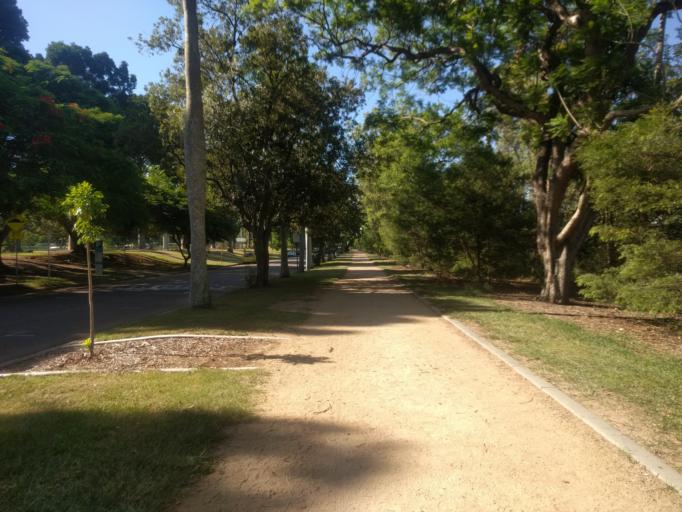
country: AU
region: Queensland
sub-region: Brisbane
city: Yeronga
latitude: -27.4997
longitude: 153.0201
